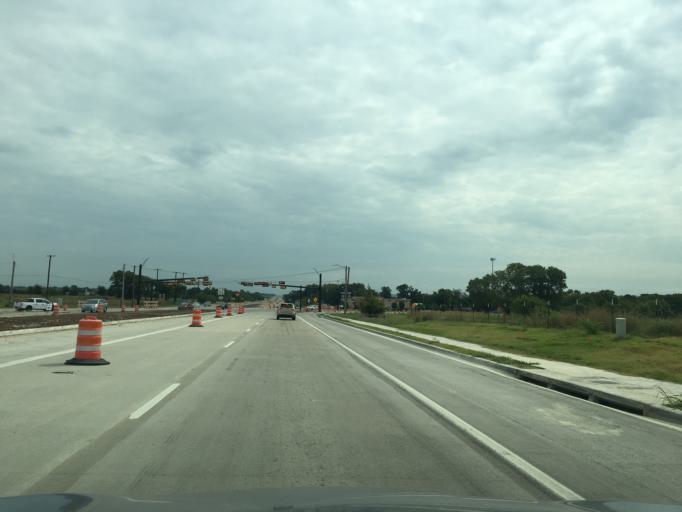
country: US
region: Texas
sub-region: Collin County
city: Melissa
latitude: 33.2817
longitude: -96.5640
